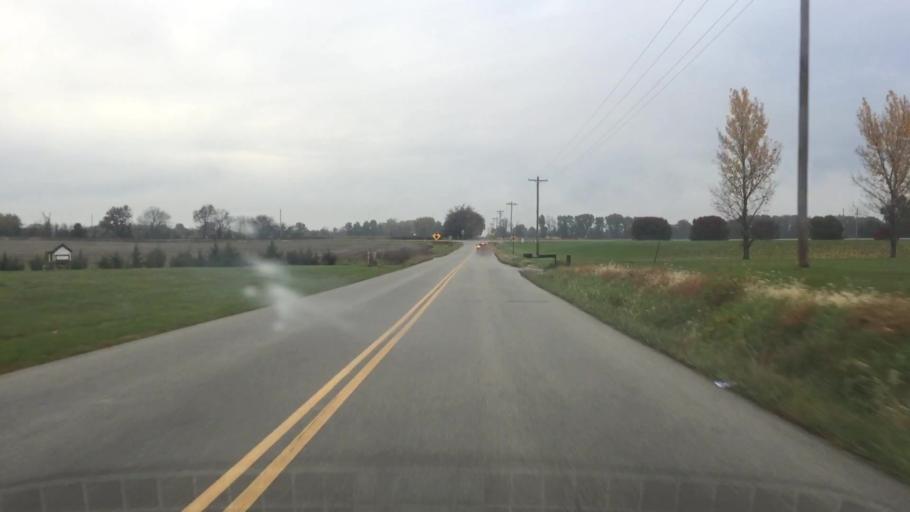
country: US
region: Missouri
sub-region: Boone County
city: Columbia
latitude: 38.9182
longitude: -92.2007
